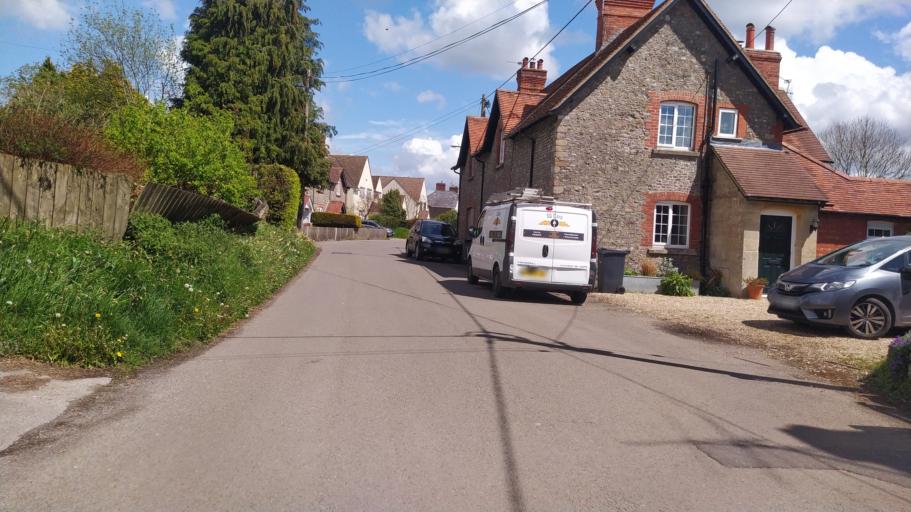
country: GB
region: England
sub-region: Wiltshire
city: Kilmington
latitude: 51.1507
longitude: -2.2838
